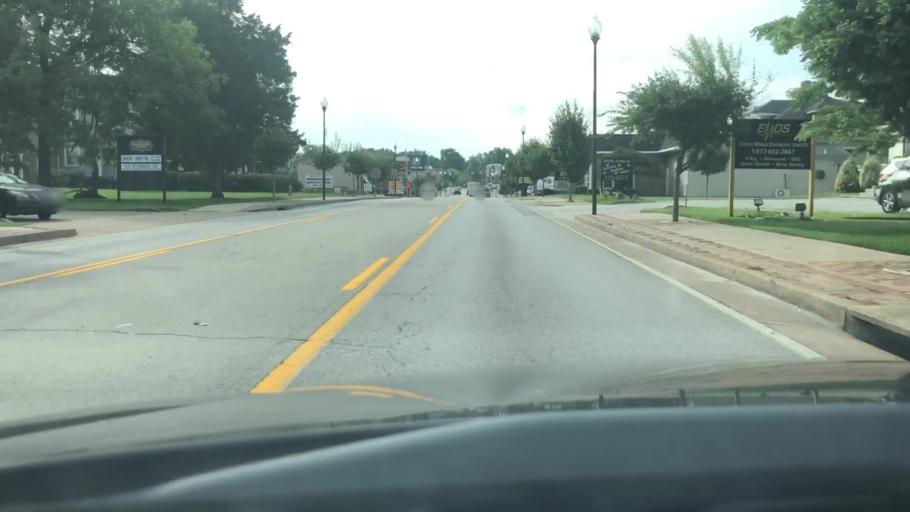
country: US
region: Kentucky
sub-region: Jefferson County
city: Lyndon
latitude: 38.2608
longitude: -85.6059
